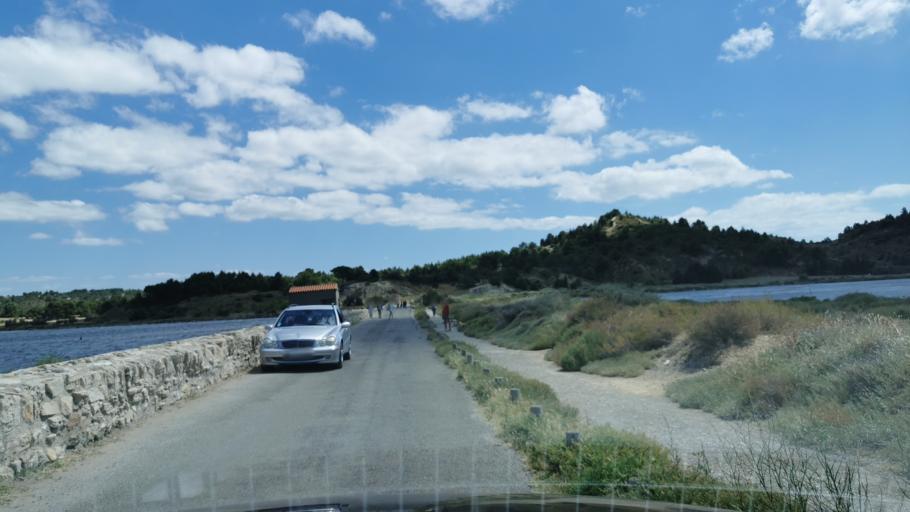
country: FR
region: Languedoc-Roussillon
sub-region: Departement de l'Aude
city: Peyriac-de-Mer
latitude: 43.0852
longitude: 2.9650
